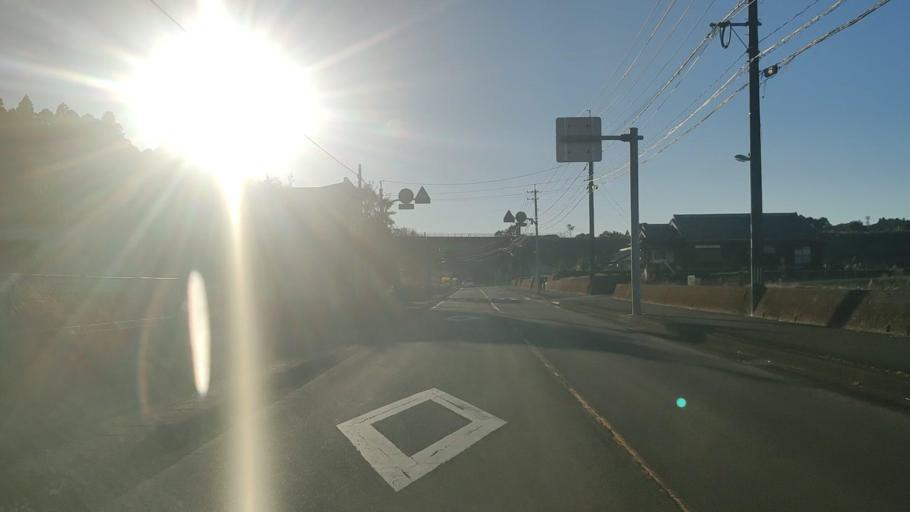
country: JP
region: Miyazaki
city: Miyazaki-shi
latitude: 31.8535
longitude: 131.3596
